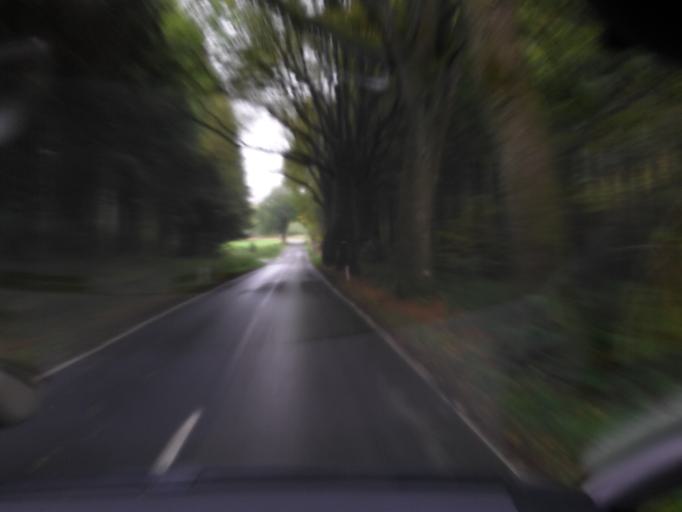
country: BE
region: Wallonia
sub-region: Province du Luxembourg
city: Neufchateau
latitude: 49.7657
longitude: 5.4165
